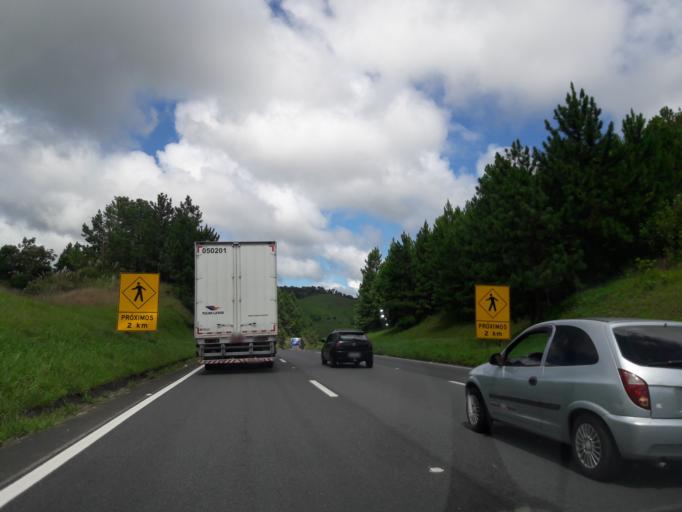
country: BR
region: Sao Paulo
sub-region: Cajati
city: Cajati
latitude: -24.9718
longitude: -48.5010
